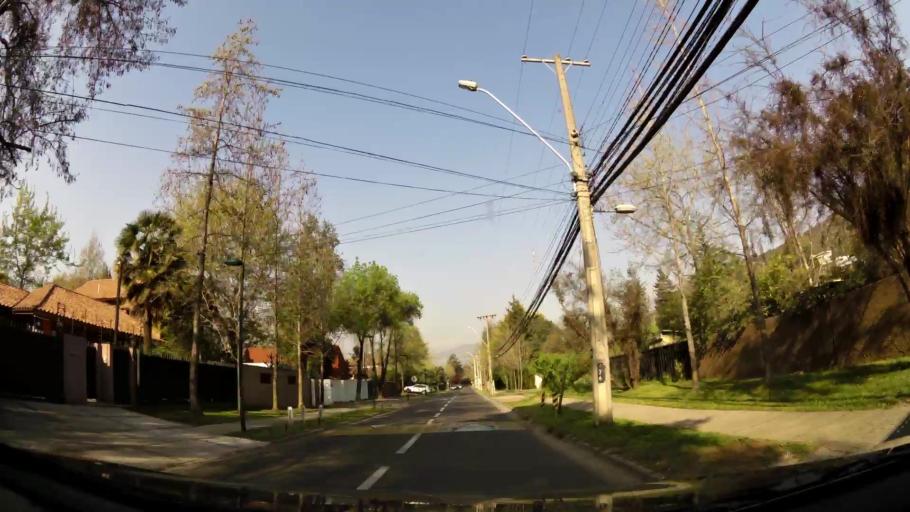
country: CL
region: Santiago Metropolitan
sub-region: Provincia de Santiago
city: Villa Presidente Frei, Nunoa, Santiago, Chile
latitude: -33.3655
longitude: -70.5307
